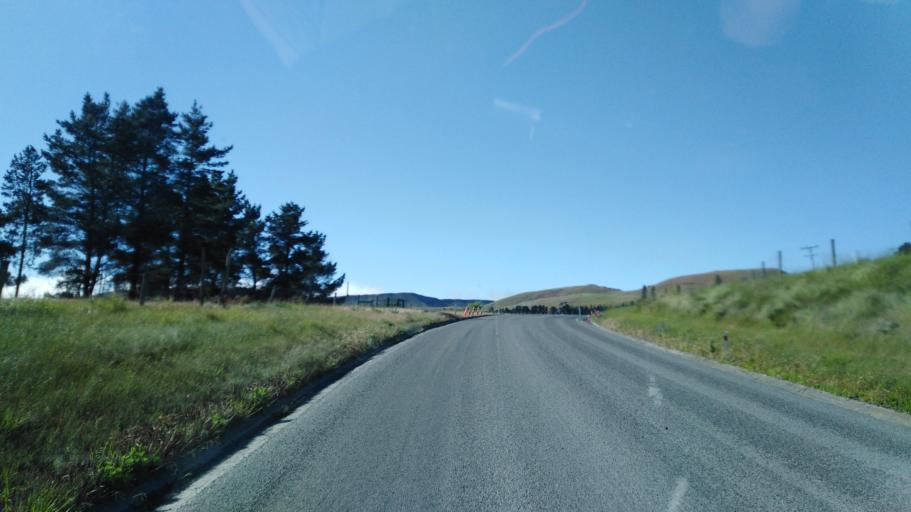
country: NZ
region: Canterbury
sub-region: Hurunui District
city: Amberley
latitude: -42.9730
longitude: 172.7064
